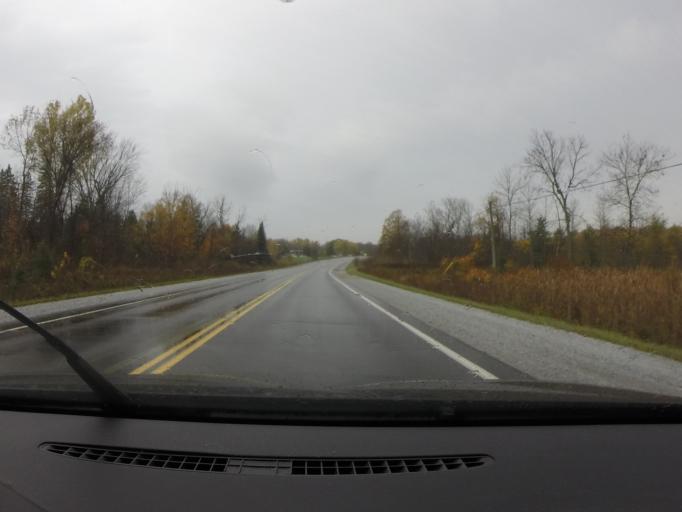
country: CA
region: Ontario
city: Perth
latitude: 44.8362
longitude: -76.5252
